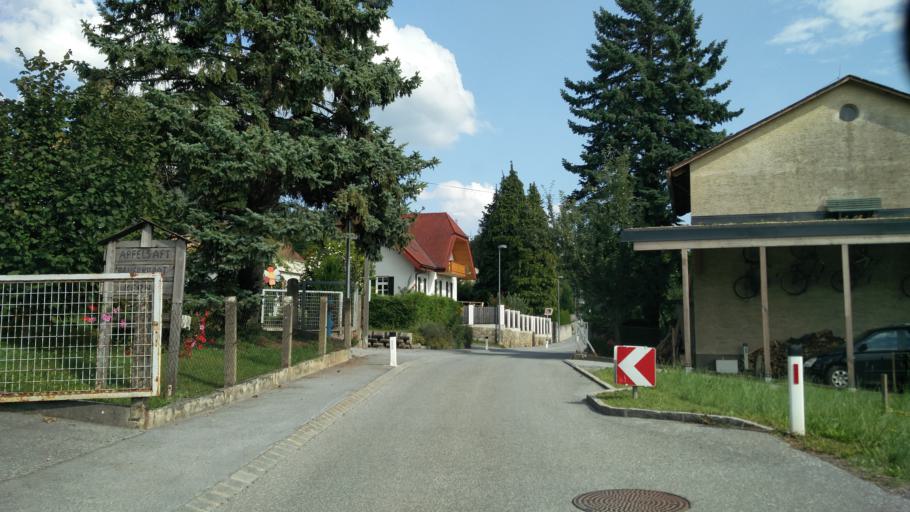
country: AT
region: Styria
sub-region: Politischer Bezirk Weiz
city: Weiz
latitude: 47.2245
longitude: 15.6287
